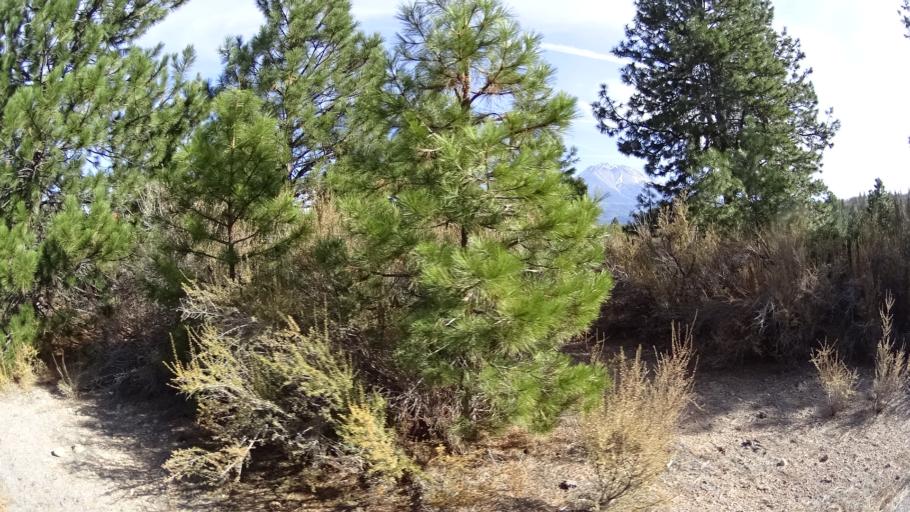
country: US
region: California
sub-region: Siskiyou County
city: Weed
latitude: 41.4240
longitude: -122.3991
